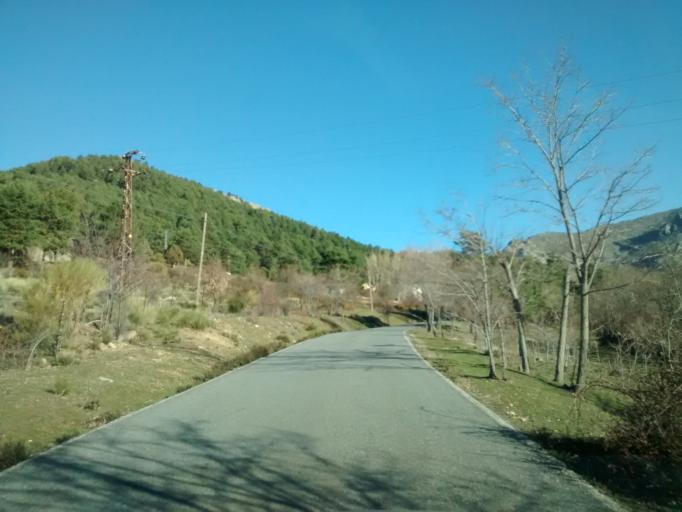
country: ES
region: Madrid
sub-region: Provincia de Madrid
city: Navacerrada
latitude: 40.7413
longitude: -4.0039
